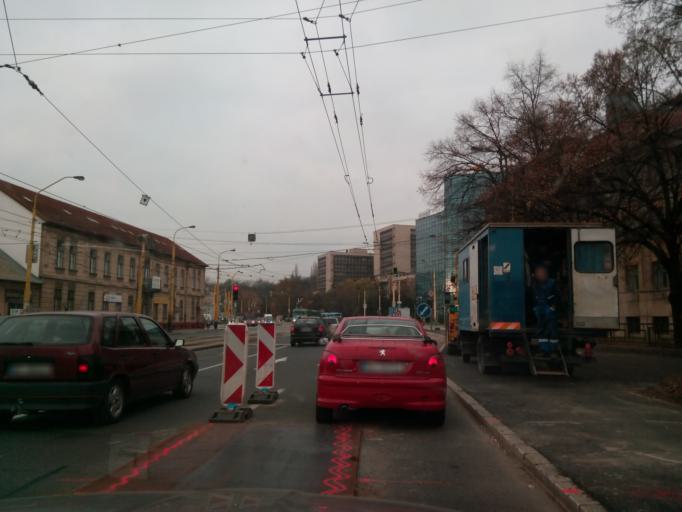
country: SK
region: Kosicky
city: Kosice
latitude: 48.7166
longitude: 21.2522
